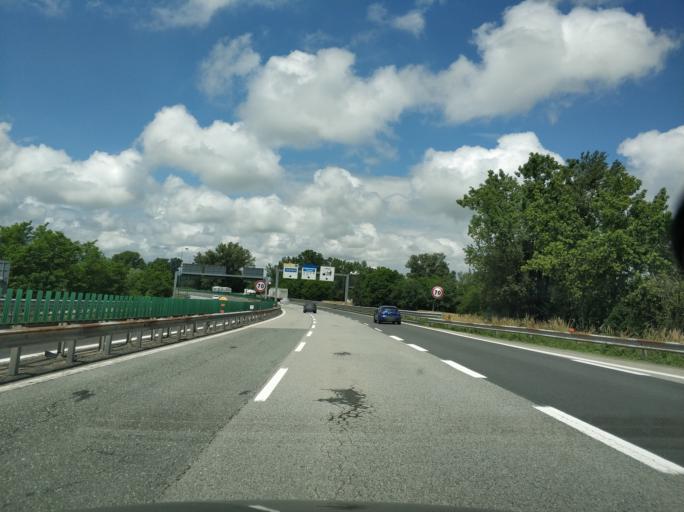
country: IT
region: Piedmont
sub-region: Provincia di Torino
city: Settimo Torinese
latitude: 45.1358
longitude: 7.7266
